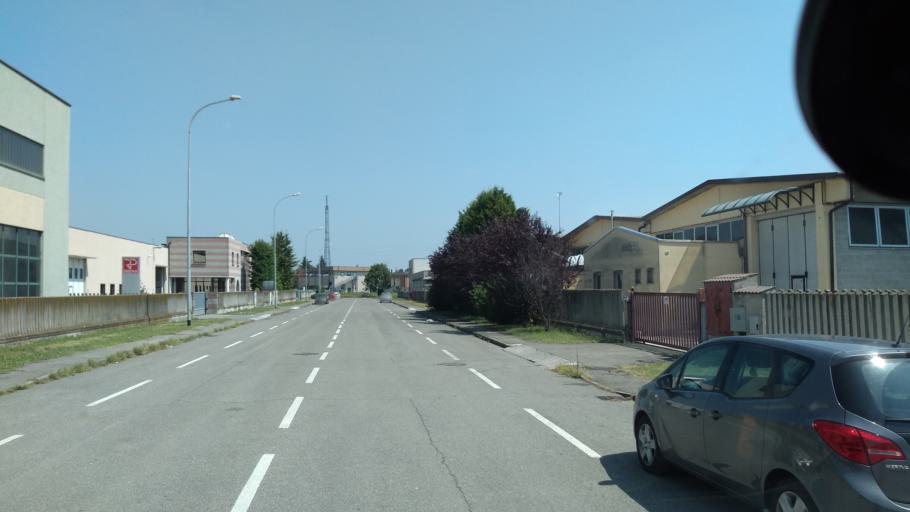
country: IT
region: Lombardy
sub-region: Provincia di Bergamo
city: Casirate d'Adda
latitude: 45.5119
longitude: 9.5723
